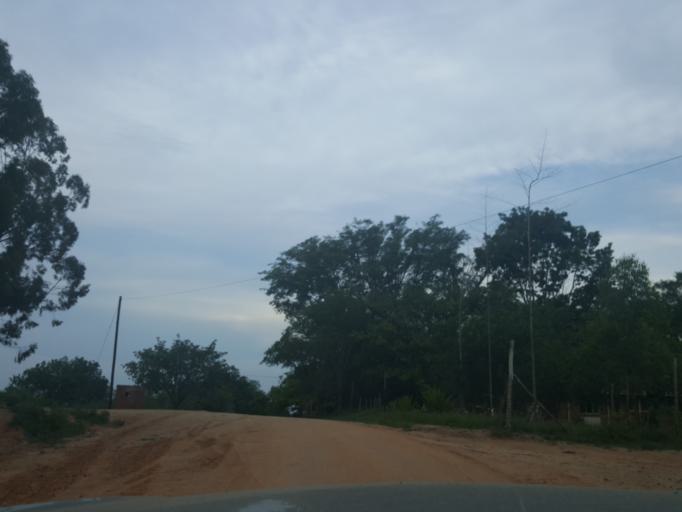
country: ZA
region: Limpopo
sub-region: Mopani District Municipality
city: Hoedspruit
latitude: -24.5929
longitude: 30.9397
